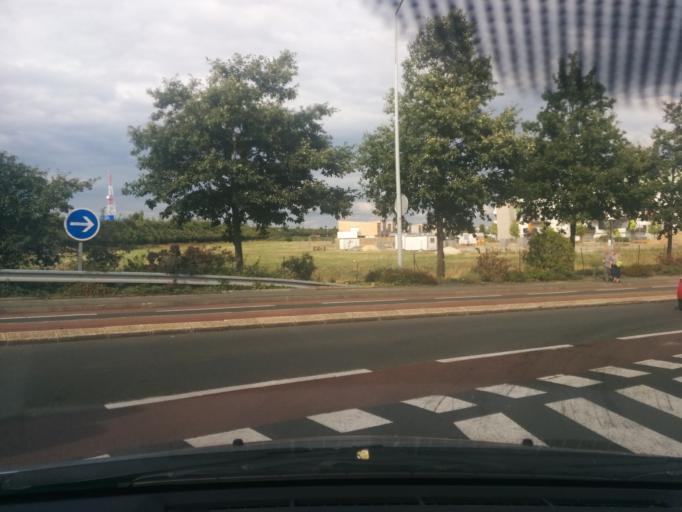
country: FR
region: Pays de la Loire
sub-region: Departement de Maine-et-Loire
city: Angers
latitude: 47.4695
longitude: -0.5115
